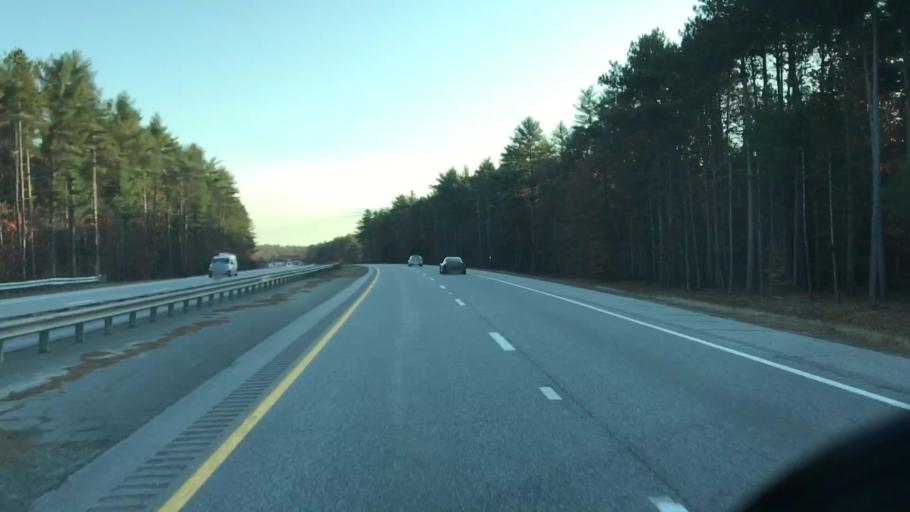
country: US
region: Maine
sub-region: Cumberland County
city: New Gloucester
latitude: 43.9971
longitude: -70.3088
